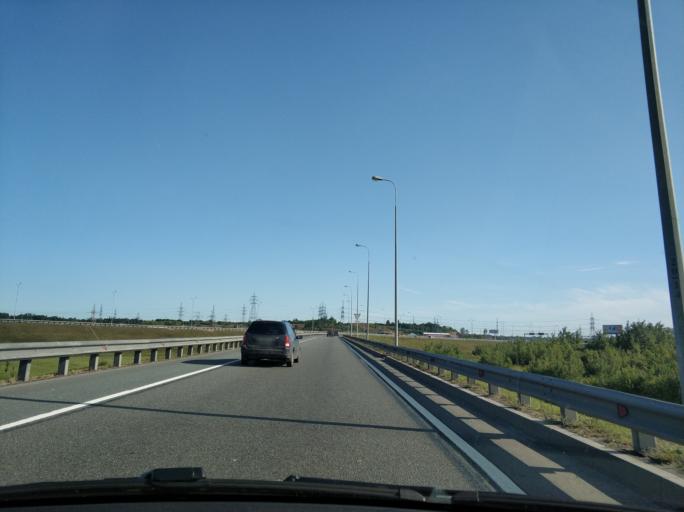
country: RU
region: Leningrad
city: Bugry
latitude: 60.0914
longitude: 30.3724
